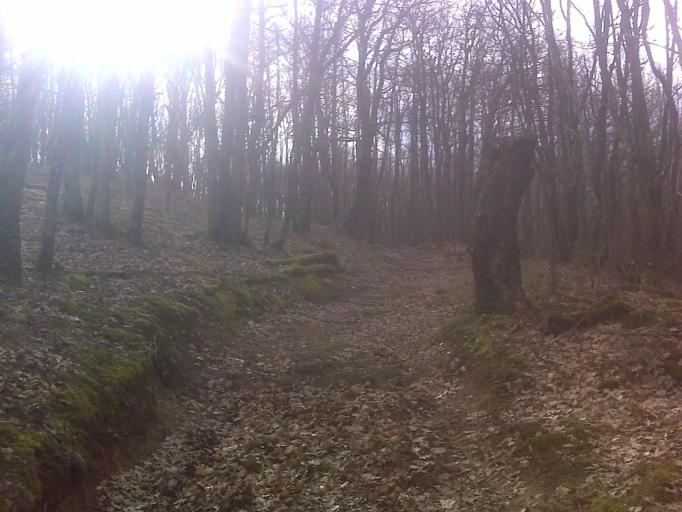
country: FR
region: Rhone-Alpes
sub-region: Departement du Rhone
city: Lentilly
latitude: 45.7951
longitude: 4.6516
